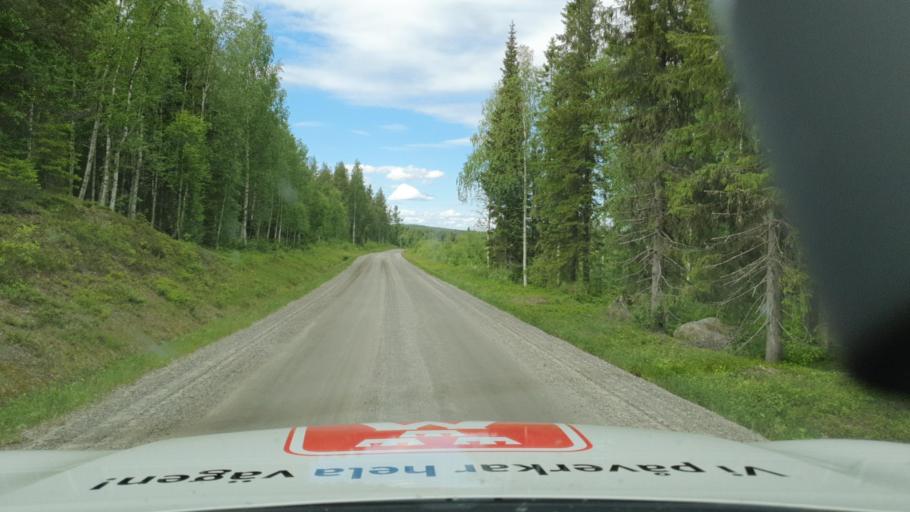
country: SE
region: Vaesterbotten
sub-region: Norsjo Kommun
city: Norsjoe
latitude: 64.8375
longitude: 19.7039
